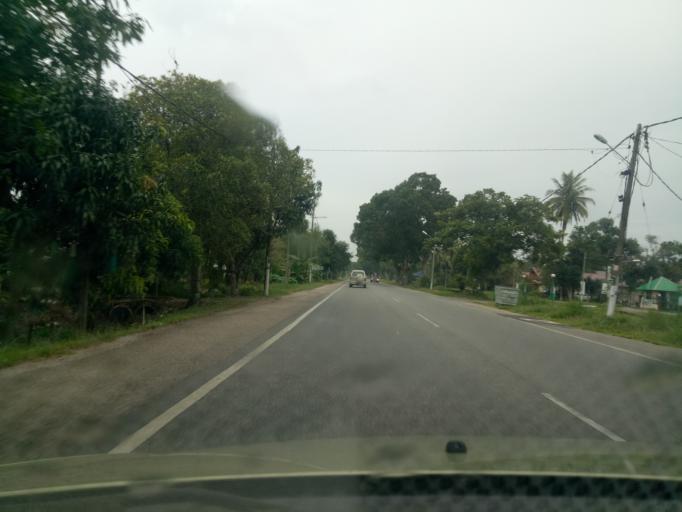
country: MY
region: Kedah
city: Gurun
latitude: 5.9107
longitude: 100.4295
